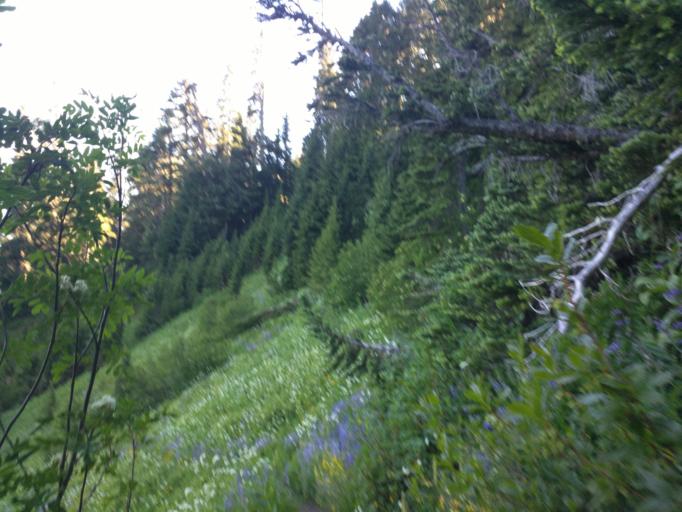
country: CA
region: British Columbia
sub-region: Fraser Valley Regional District
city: Chilliwack
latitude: 48.9268
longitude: -121.8677
